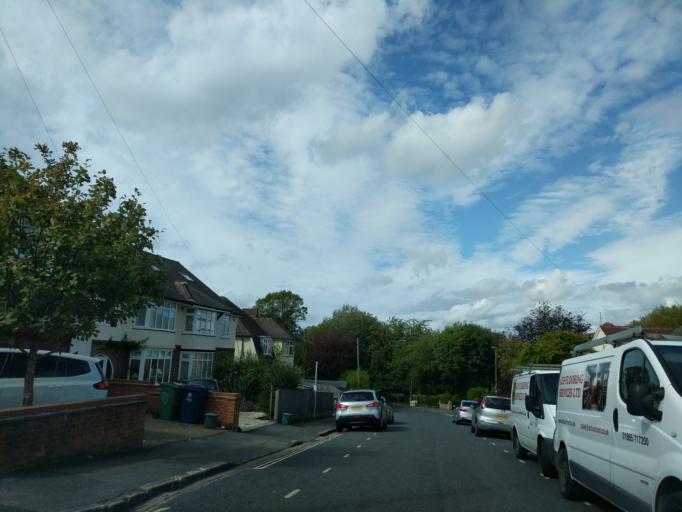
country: GB
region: England
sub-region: Oxfordshire
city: Cowley
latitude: 51.7633
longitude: -1.2219
